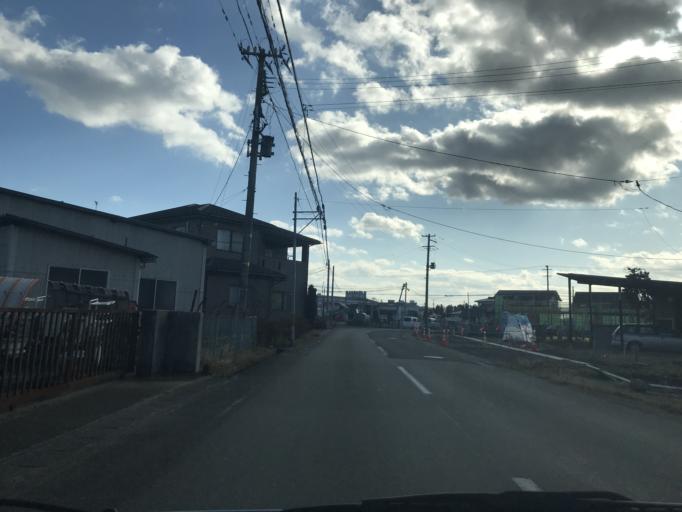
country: JP
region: Iwate
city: Ichinoseki
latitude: 38.7553
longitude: 141.0651
